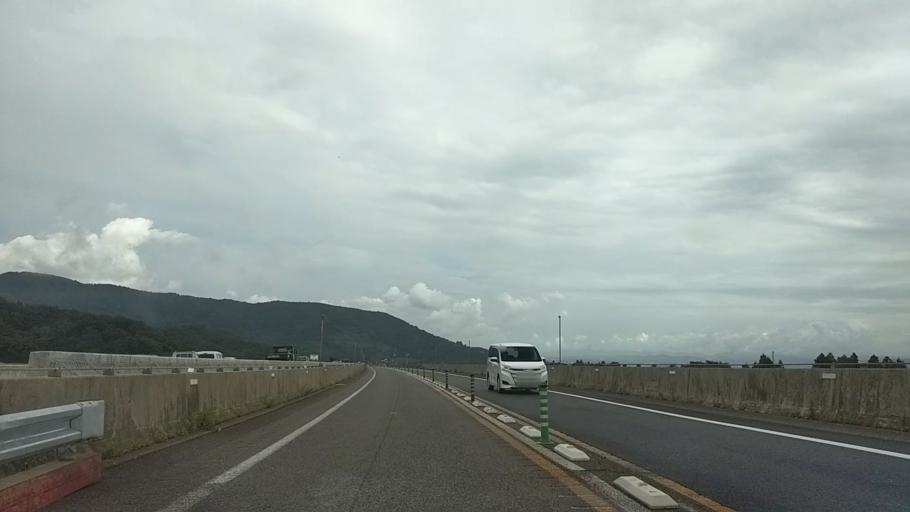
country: JP
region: Niigata
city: Arai
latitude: 37.0125
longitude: 138.2138
